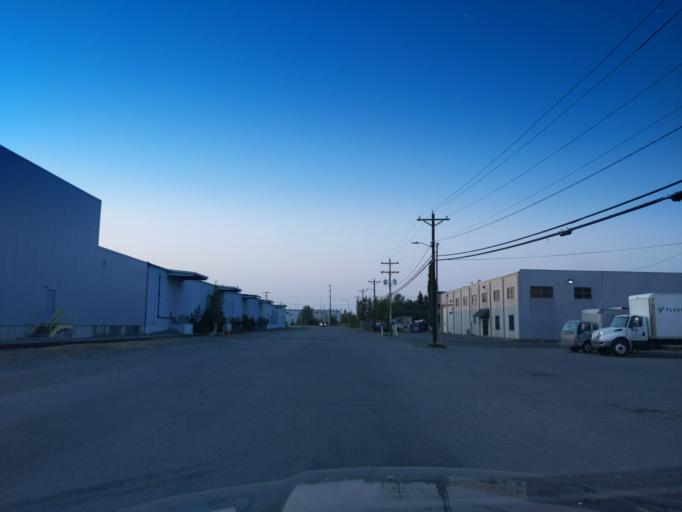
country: US
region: Alaska
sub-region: Anchorage Municipality
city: Anchorage
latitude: 61.1623
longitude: -149.8958
